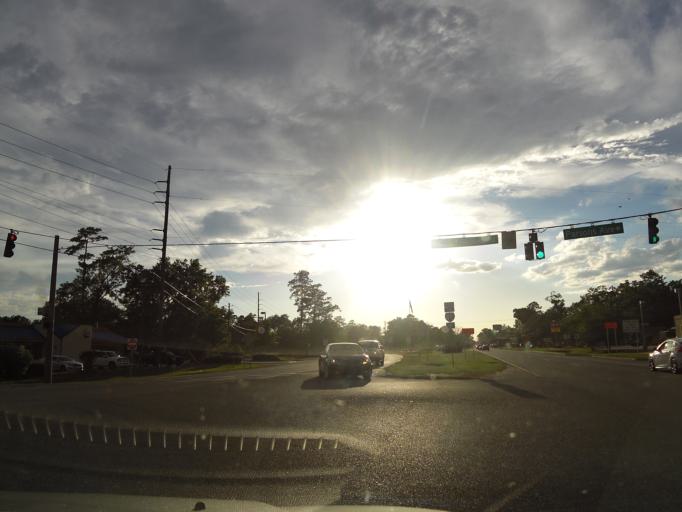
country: US
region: Georgia
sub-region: Chatham County
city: Pooler
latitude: 32.1134
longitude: -81.2406
